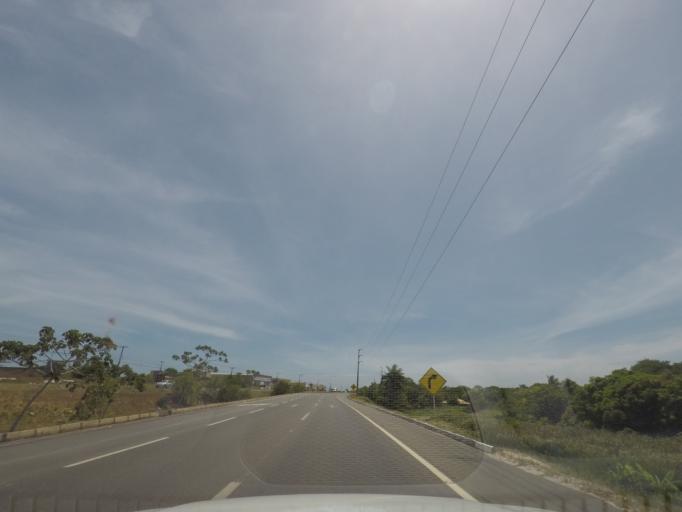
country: BR
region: Bahia
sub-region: Camacari
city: Camacari
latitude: -12.6564
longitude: -38.0878
